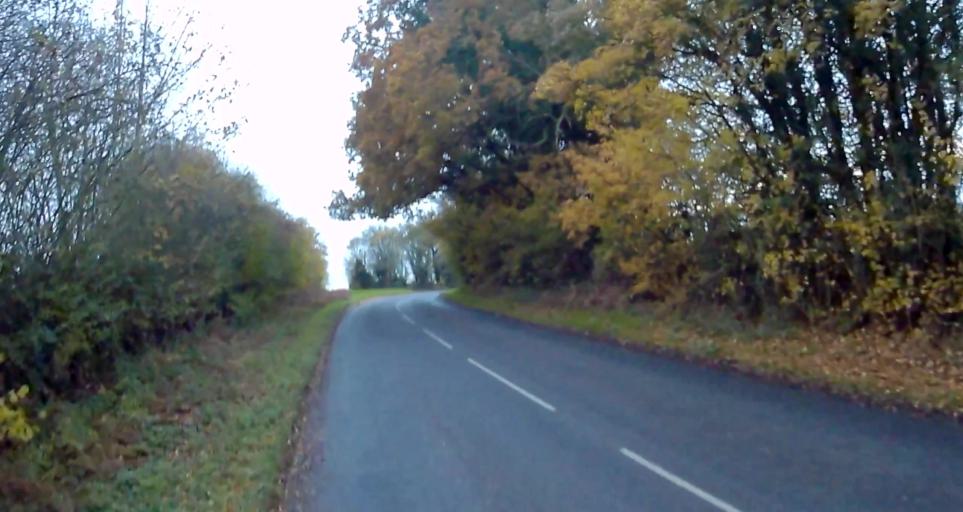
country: GB
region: England
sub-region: Hampshire
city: Odiham
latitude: 51.2426
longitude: -0.9770
